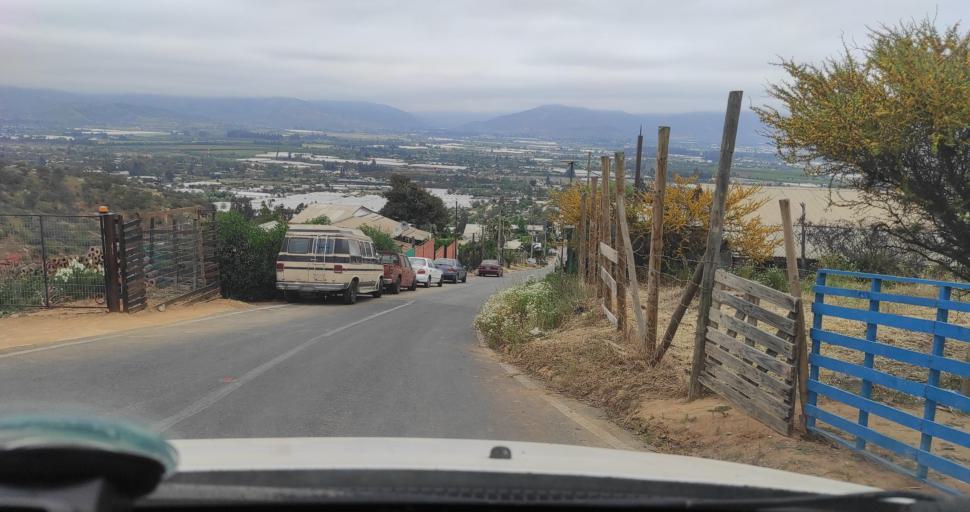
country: CL
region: Valparaiso
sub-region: Provincia de Marga Marga
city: Limache
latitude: -32.9838
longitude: -71.2243
